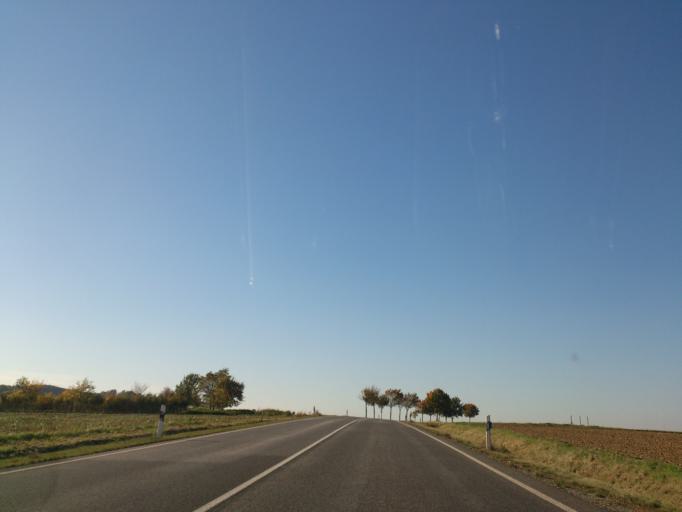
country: DE
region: Hesse
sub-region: Regierungsbezirk Kassel
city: Breuna
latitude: 51.4548
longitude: 9.2330
